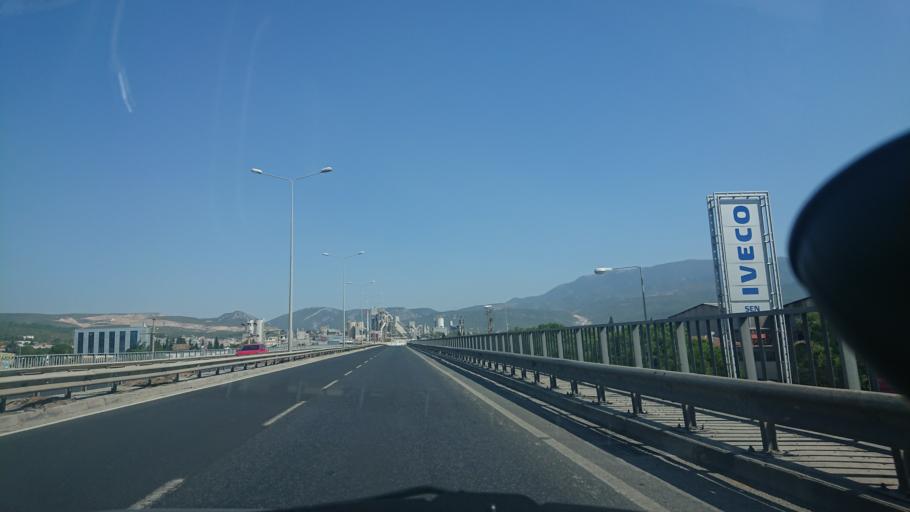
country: TR
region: Izmir
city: Bornova
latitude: 38.4580
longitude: 27.2486
